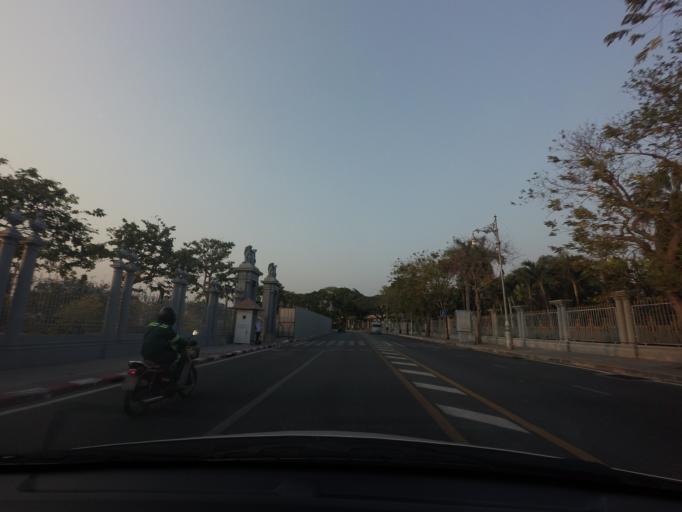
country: TH
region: Bangkok
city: Dusit
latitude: 13.7708
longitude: 100.5147
